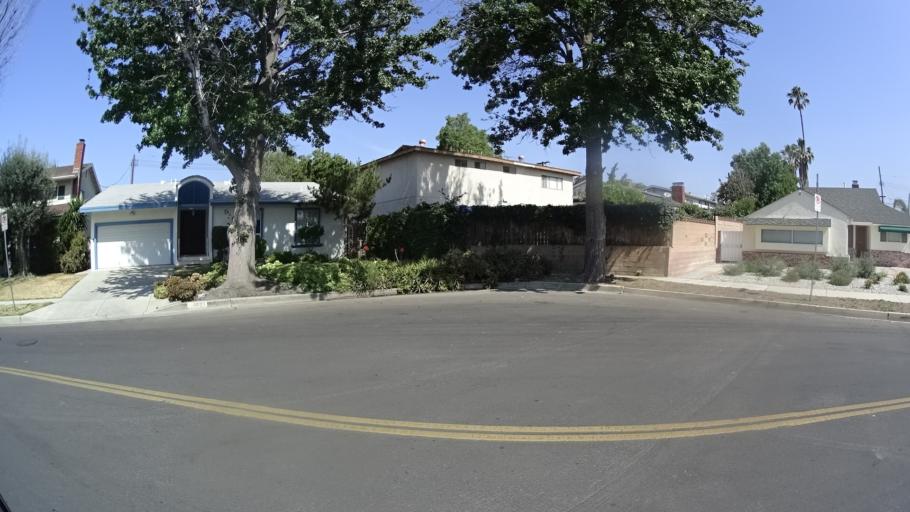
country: US
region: California
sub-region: Los Angeles County
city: Van Nuys
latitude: 34.1964
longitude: -118.4551
